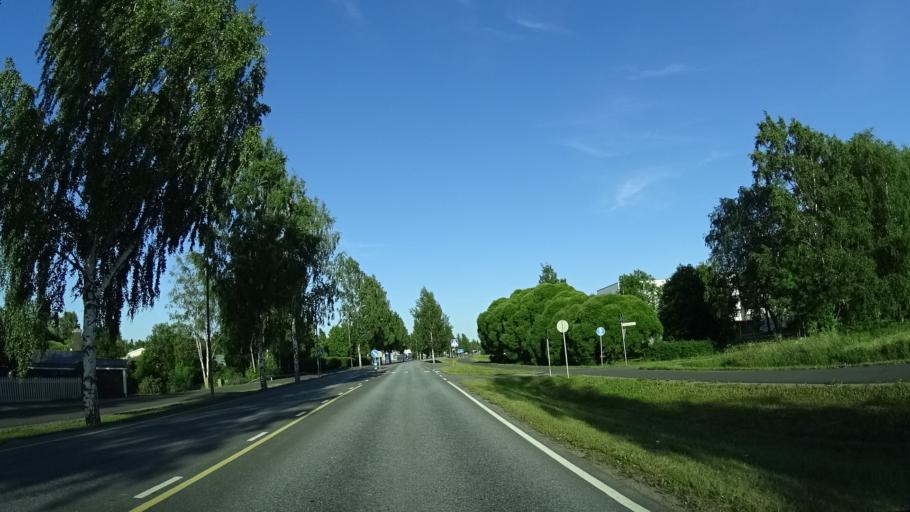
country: FI
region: Satakunta
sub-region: Pori
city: Kokemaeki
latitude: 61.2576
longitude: 22.3350
